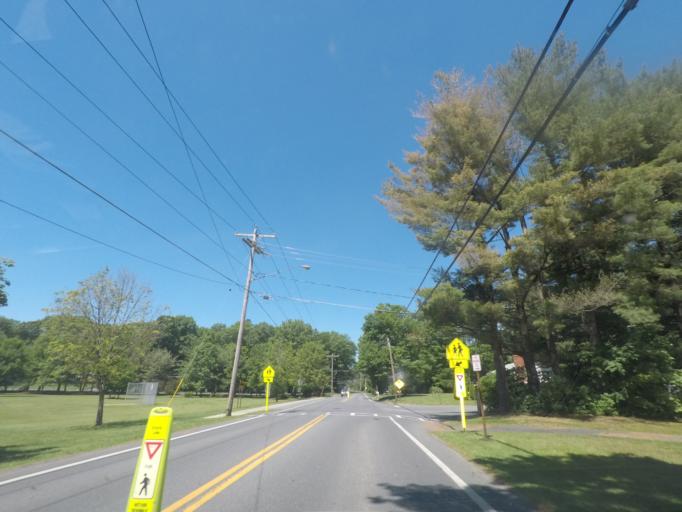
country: US
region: New York
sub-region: Saratoga County
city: Country Knolls
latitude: 42.8577
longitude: -73.8093
